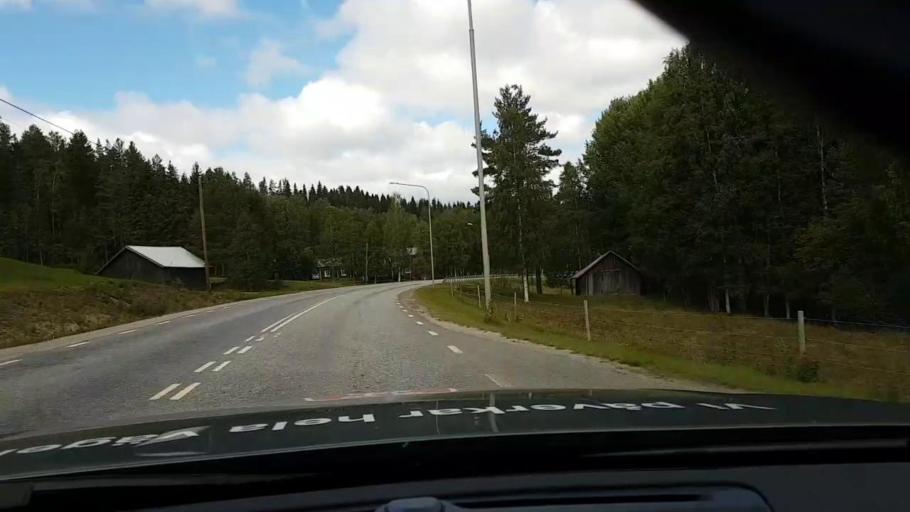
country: SE
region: Vaesternorrland
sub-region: OErnskoeldsviks Kommun
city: Bredbyn
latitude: 63.4914
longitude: 18.0808
